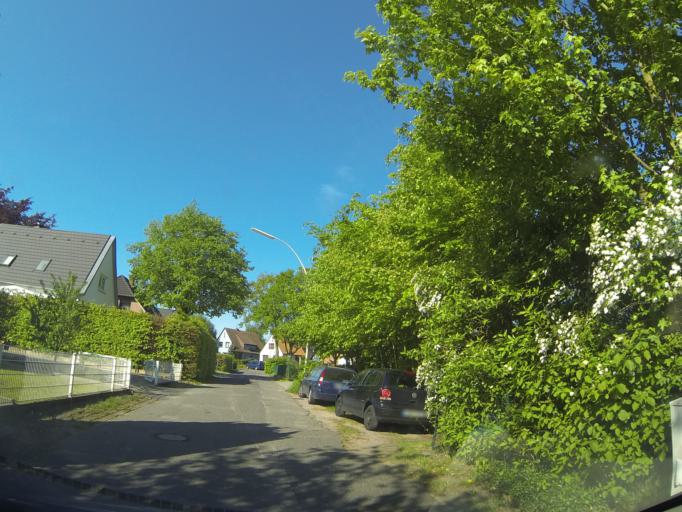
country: DE
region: Schleswig-Holstein
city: Halstenbek
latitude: 53.6316
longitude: 9.8350
